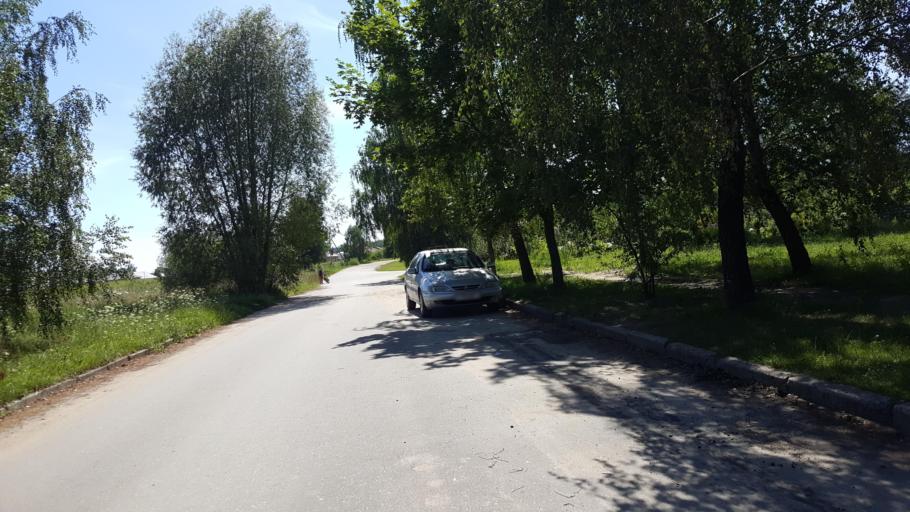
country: BY
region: Brest
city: Charnawchytsy
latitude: 52.2624
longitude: 23.5933
